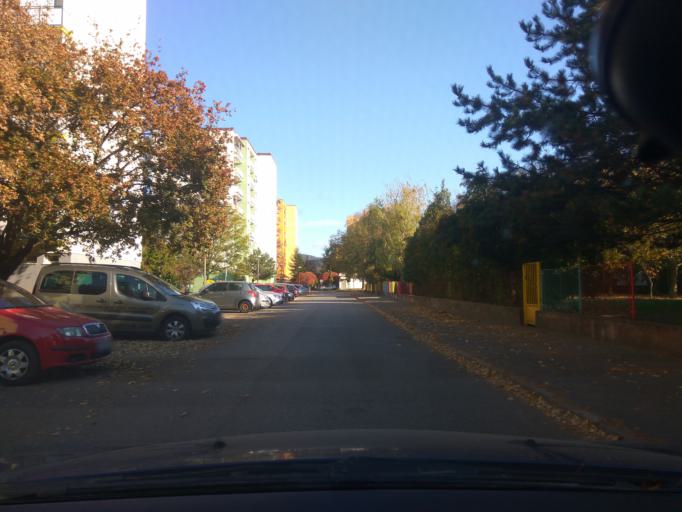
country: SK
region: Trnavsky
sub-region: Okres Trnava
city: Piestany
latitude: 48.5863
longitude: 17.8200
